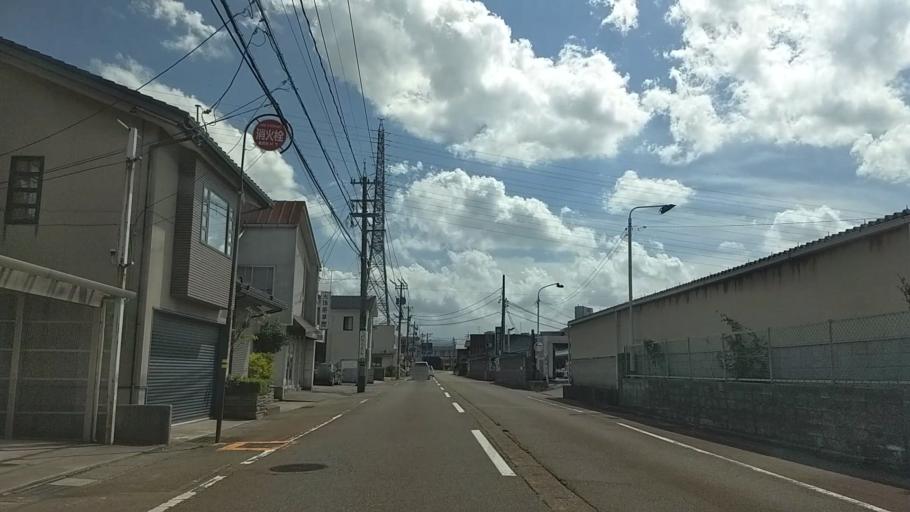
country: JP
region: Ishikawa
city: Kanazawa-shi
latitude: 36.5900
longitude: 136.6496
